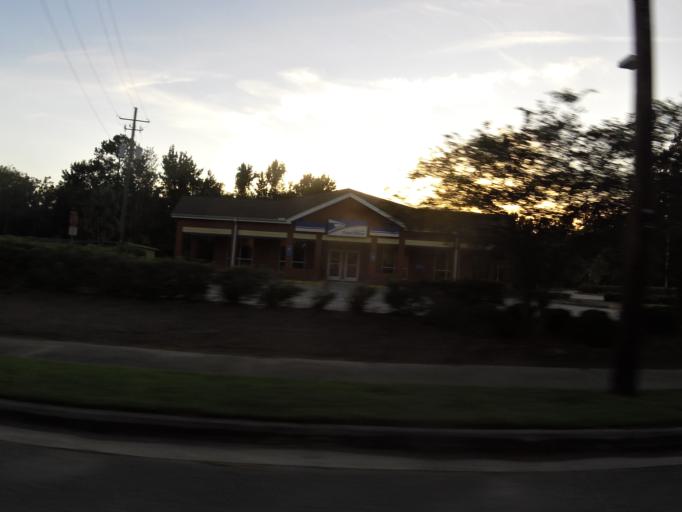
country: US
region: Georgia
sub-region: Camden County
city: Woodbine
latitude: 30.9700
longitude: -81.7242
